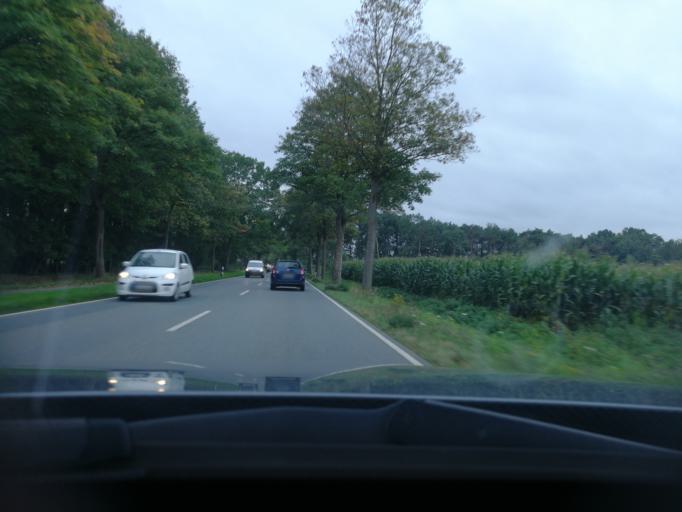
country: DE
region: North Rhine-Westphalia
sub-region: Regierungsbezirk Dusseldorf
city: Kevelaer
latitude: 51.5256
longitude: 6.2424
